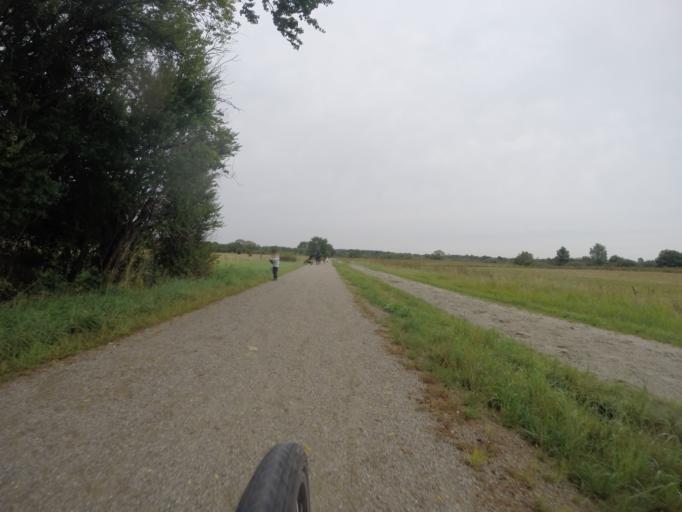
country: DK
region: Capital Region
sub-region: Herlev Kommune
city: Herlev
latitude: 55.7474
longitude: 12.4273
